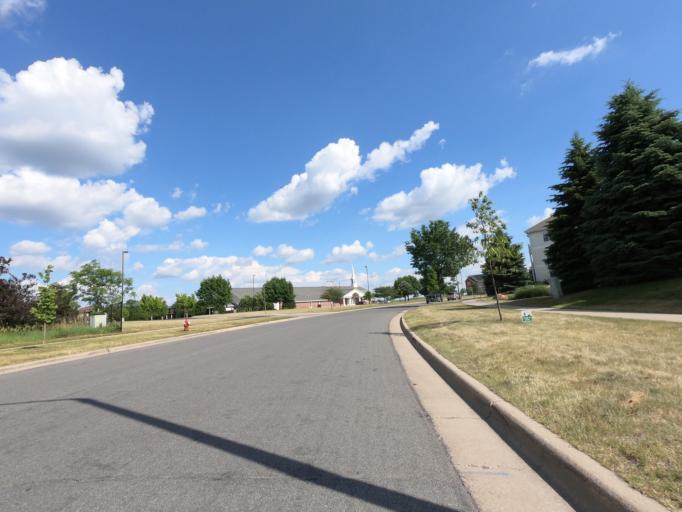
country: US
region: Wisconsin
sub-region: Dane County
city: Middleton
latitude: 43.0761
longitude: -89.5492
